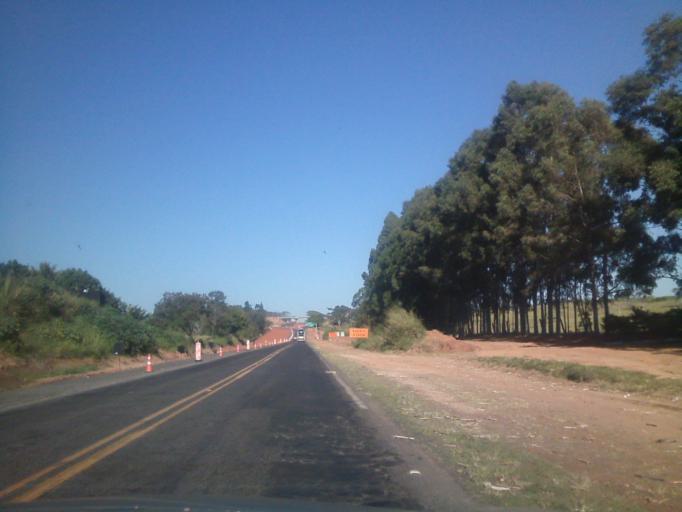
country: BR
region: Sao Paulo
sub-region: Pirapozinho
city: Pirapozinho
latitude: -22.2730
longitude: -51.5113
